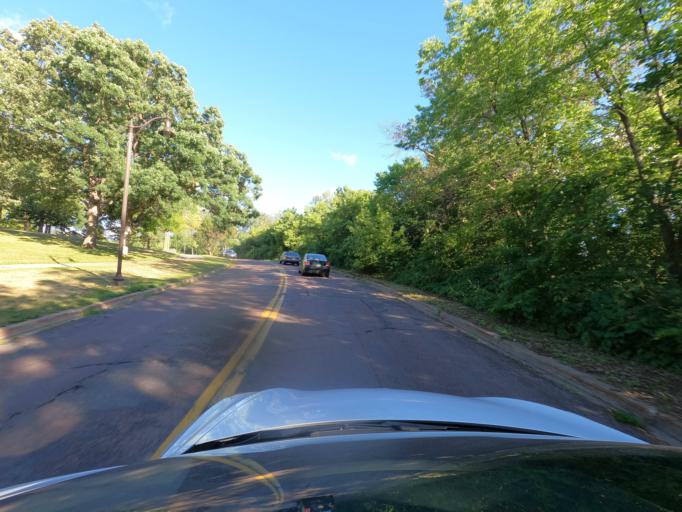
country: US
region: Minnesota
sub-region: Anoka County
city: Columbia Heights
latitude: 45.0244
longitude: -93.2436
